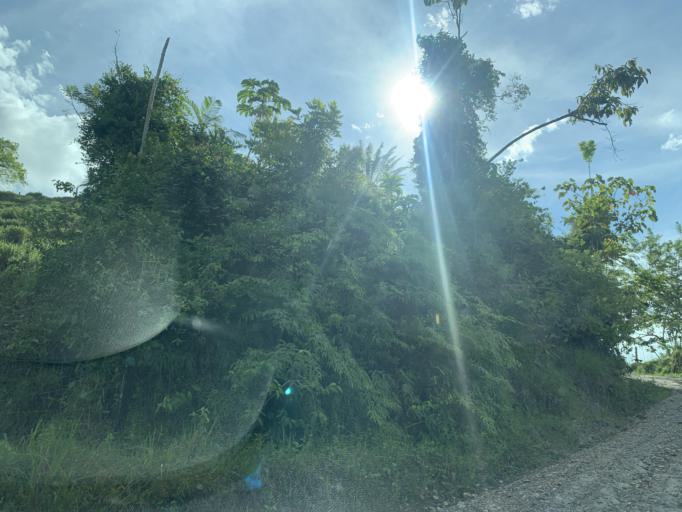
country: CO
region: Boyaca
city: Puerto Boyaca
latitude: 6.0050
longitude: -74.3814
